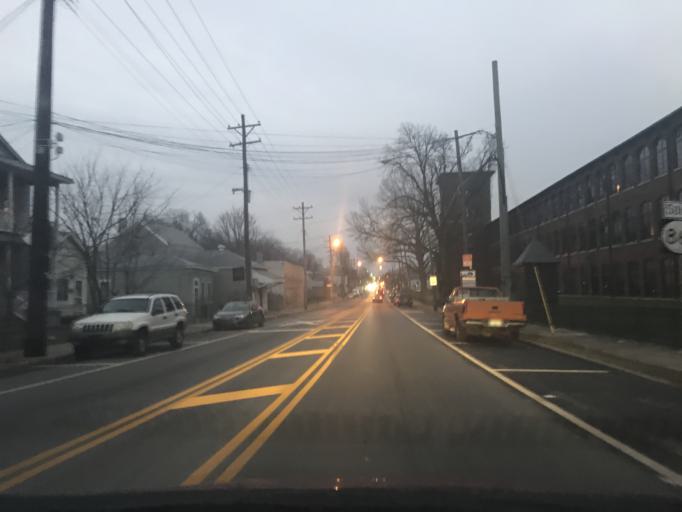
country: US
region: Kentucky
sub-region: Jefferson County
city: Audubon Park
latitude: 38.2302
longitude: -85.7401
